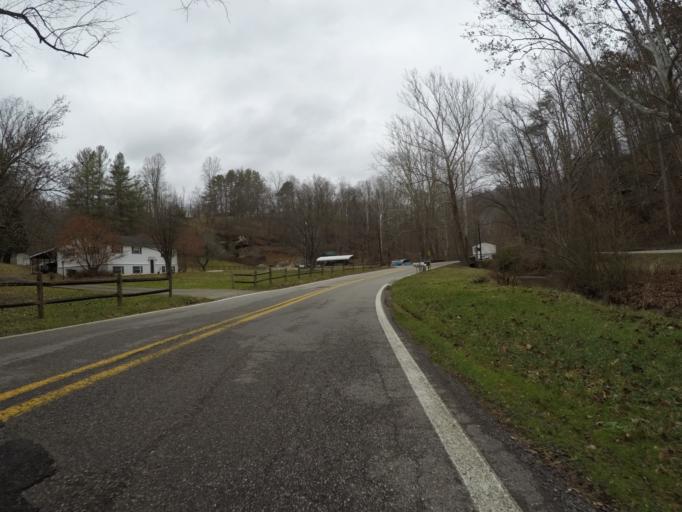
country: US
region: West Virginia
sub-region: Cabell County
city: Barboursville
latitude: 38.4429
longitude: -82.2461
